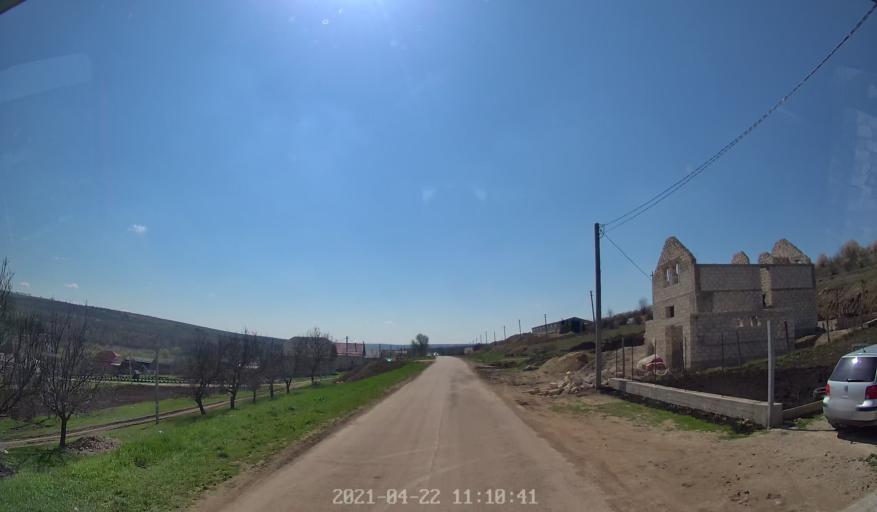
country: MD
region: Chisinau
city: Ciorescu
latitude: 47.1600
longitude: 28.9542
